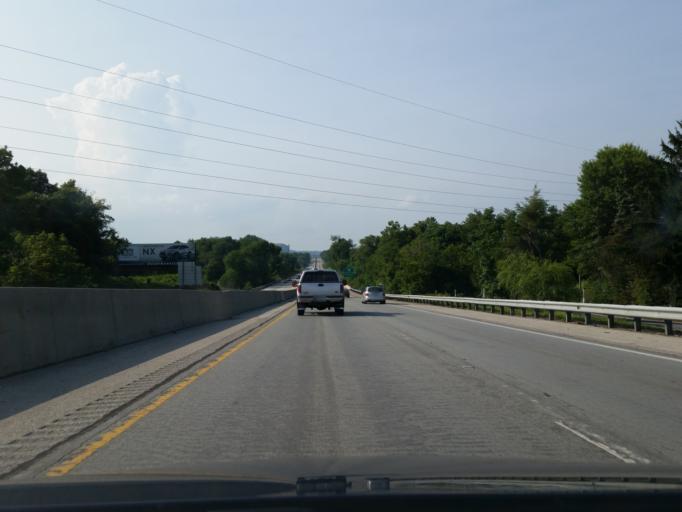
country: US
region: Pennsylvania
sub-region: York County
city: Manchester
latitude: 40.0509
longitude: -76.7518
